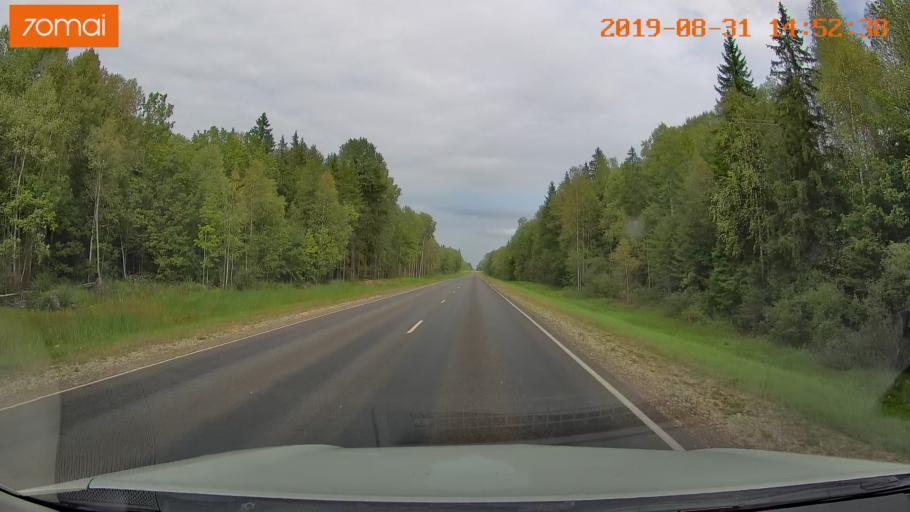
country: RU
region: Kaluga
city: Spas-Demensk
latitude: 54.2774
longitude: 33.8444
